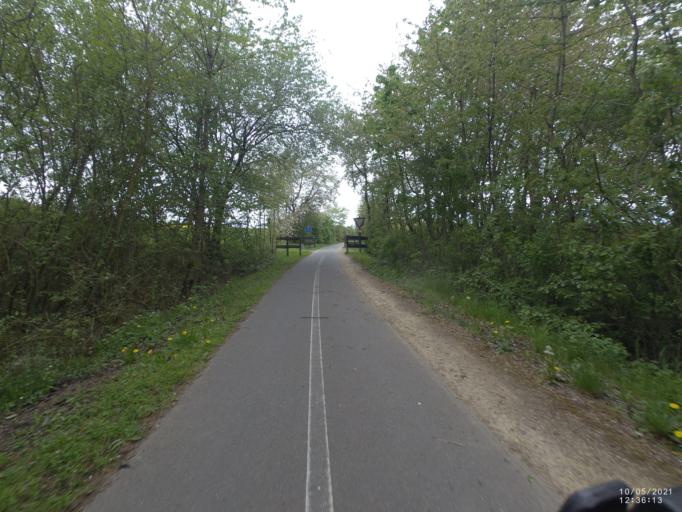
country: DE
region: Rheinland-Pfalz
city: Ruber
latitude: 50.3063
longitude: 7.3565
